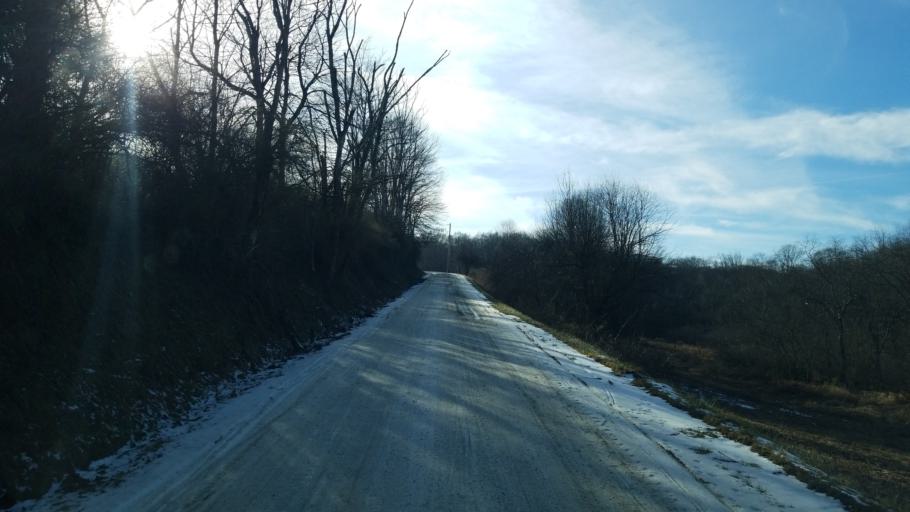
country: US
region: Pennsylvania
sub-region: Indiana County
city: Chevy Chase Heights
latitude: 40.8321
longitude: -79.1622
